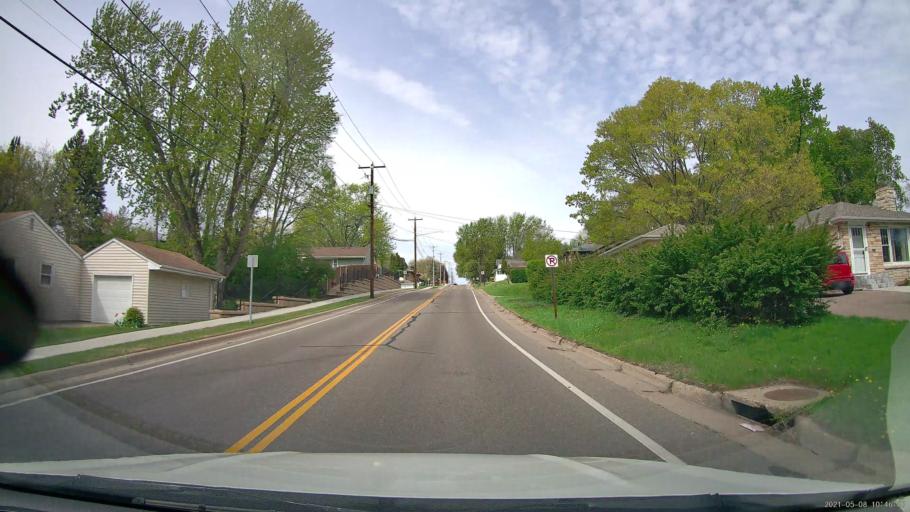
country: US
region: Minnesota
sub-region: Dakota County
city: South Saint Paul
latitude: 44.8980
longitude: -93.0553
